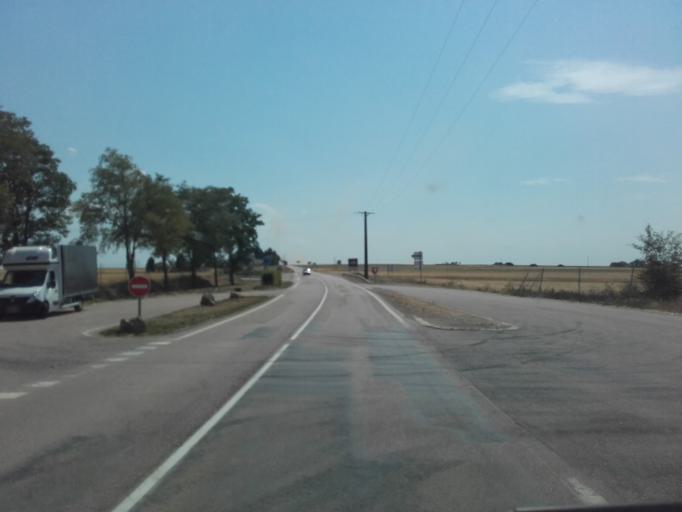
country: FR
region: Bourgogne
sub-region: Departement de l'Yonne
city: Joux-la-Ville
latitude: 47.6604
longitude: 3.8772
